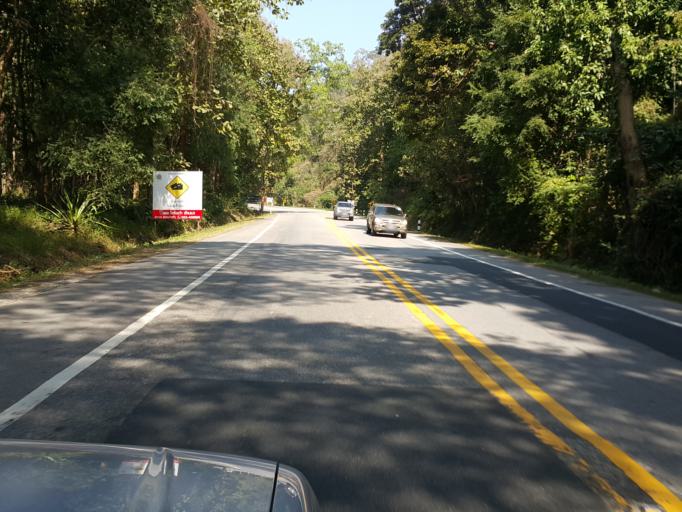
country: TH
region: Chiang Mai
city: Mae On
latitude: 18.9362
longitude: 99.2382
